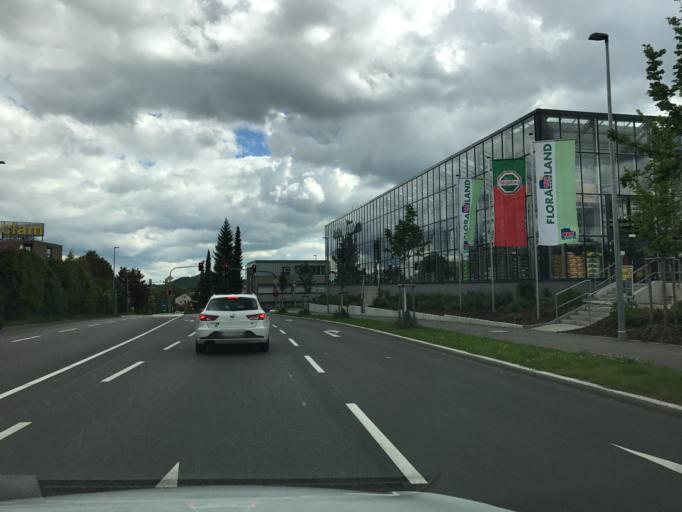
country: DE
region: Baden-Wuerttemberg
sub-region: Regierungsbezirk Stuttgart
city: Ditzingen
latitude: 48.8217
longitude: 9.0649
